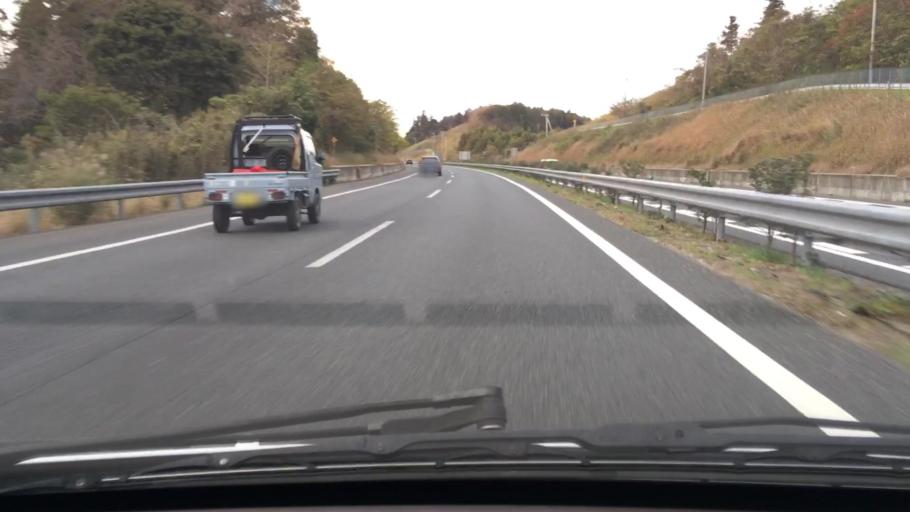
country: JP
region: Chiba
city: Kisarazu
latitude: 35.3273
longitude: 139.9463
